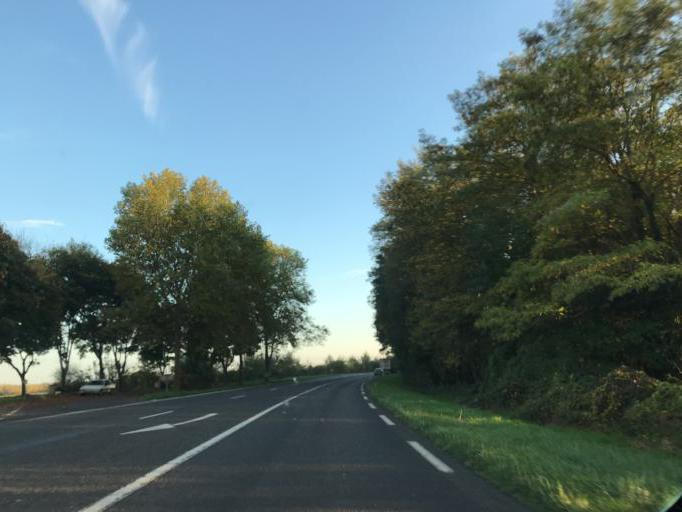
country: FR
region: Bourgogne
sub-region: Departement de l'Yonne
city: Pont-sur-Yonne
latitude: 48.2670
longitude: 3.2351
